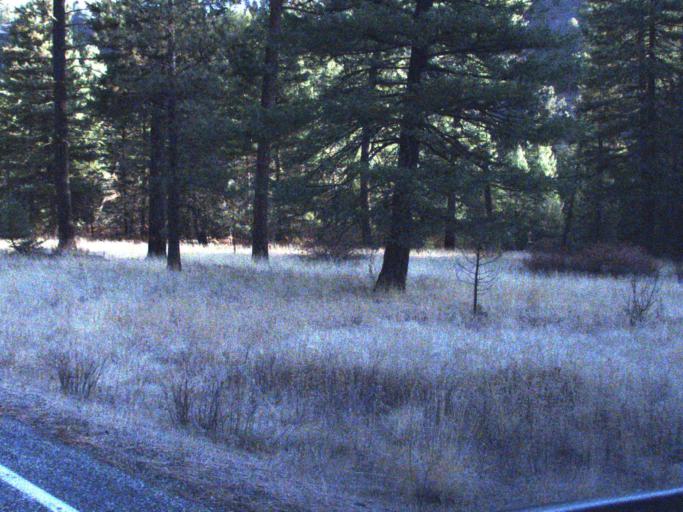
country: US
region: Washington
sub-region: Ferry County
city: Republic
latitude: 48.3575
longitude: -118.7416
